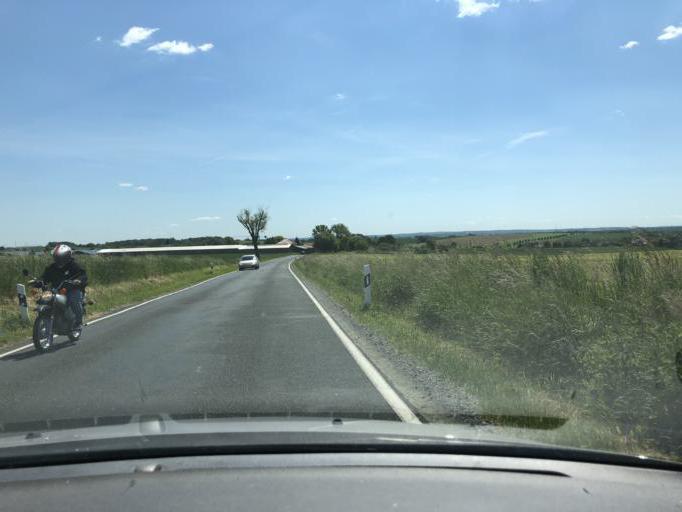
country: DE
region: Saxony
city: Nerchau
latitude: 51.2385
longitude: 12.8204
